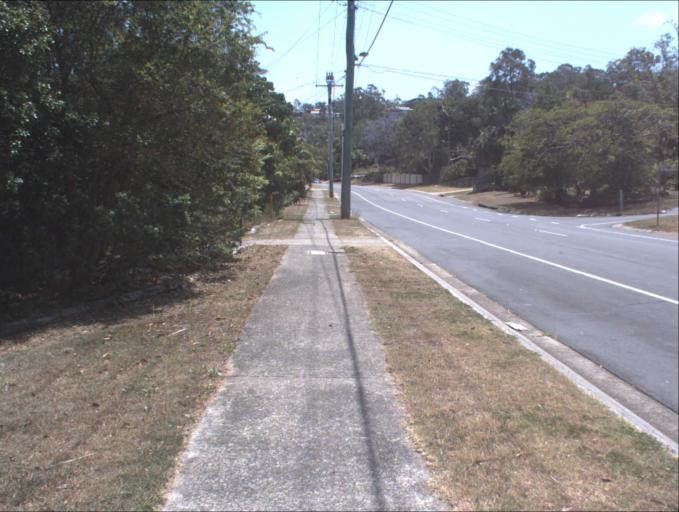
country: AU
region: Queensland
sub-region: Logan
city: Slacks Creek
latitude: -27.6640
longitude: 153.1922
